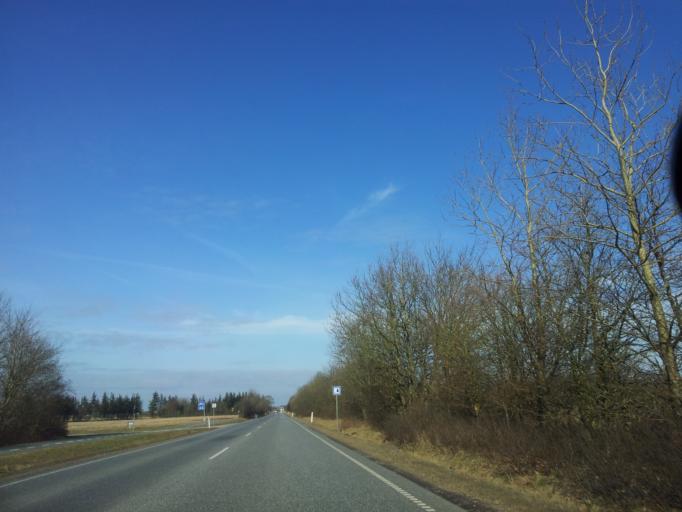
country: DK
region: South Denmark
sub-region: Esbjerg Kommune
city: Ribe
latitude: 55.3020
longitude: 8.7439
